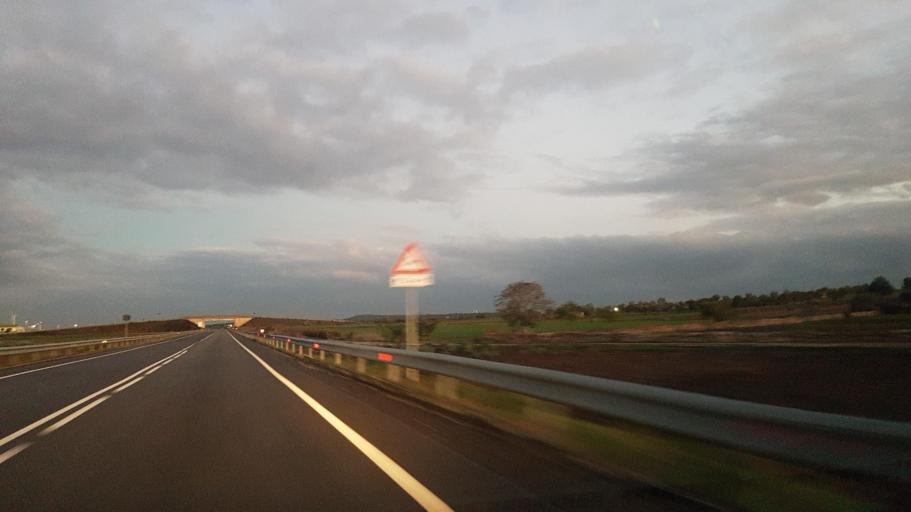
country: IT
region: Apulia
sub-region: Provincia di Taranto
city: Laterza
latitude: 40.6550
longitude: 16.7903
